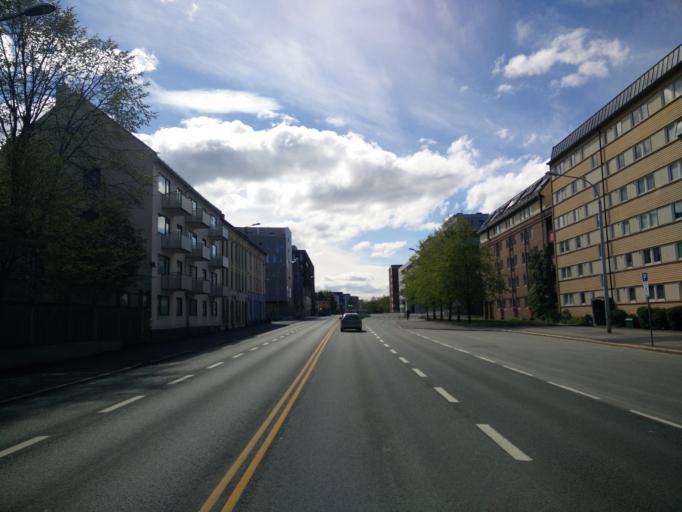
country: NO
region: Sor-Trondelag
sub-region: Trondheim
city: Trondheim
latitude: 63.4173
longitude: 10.3970
